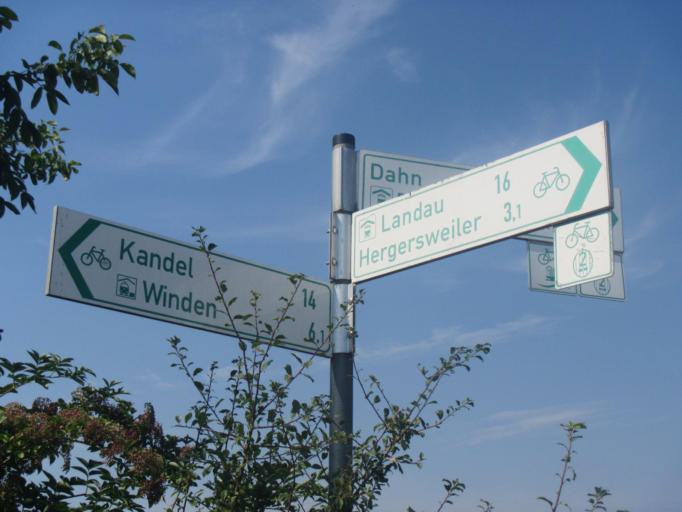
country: DE
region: Rheinland-Pfalz
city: Hergersweiler
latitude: 49.0848
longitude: 8.0843
